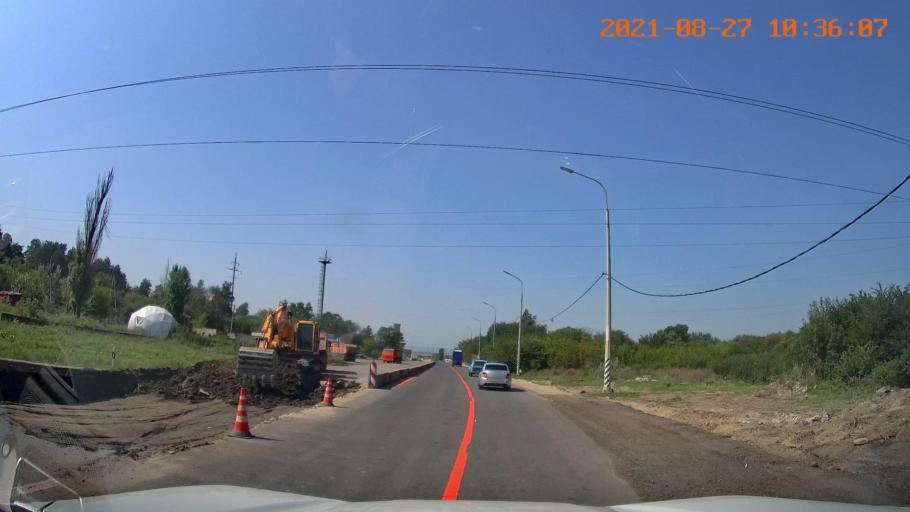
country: RU
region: Karachayevo-Cherkesiya
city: Cherkessk
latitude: 44.2528
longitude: 42.0903
